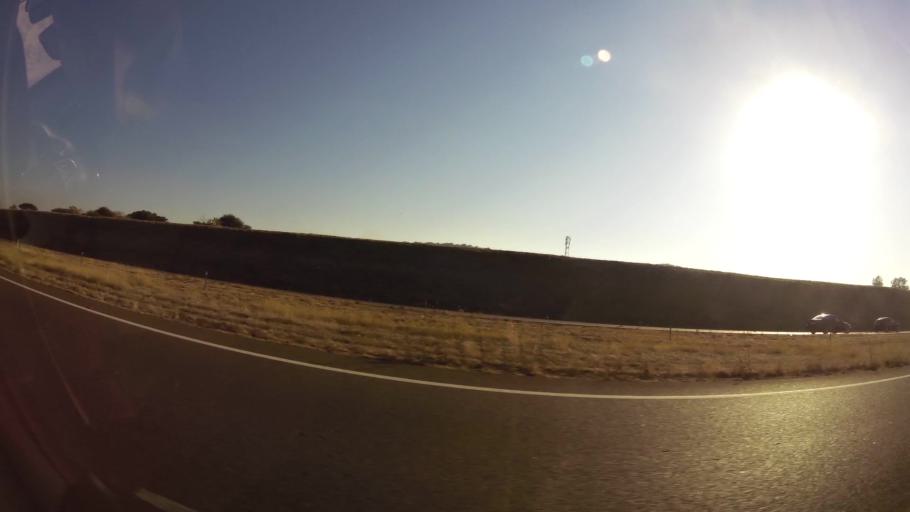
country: ZA
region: Gauteng
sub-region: City of Tshwane Metropolitan Municipality
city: Pretoria
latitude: -25.6391
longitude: 28.2113
